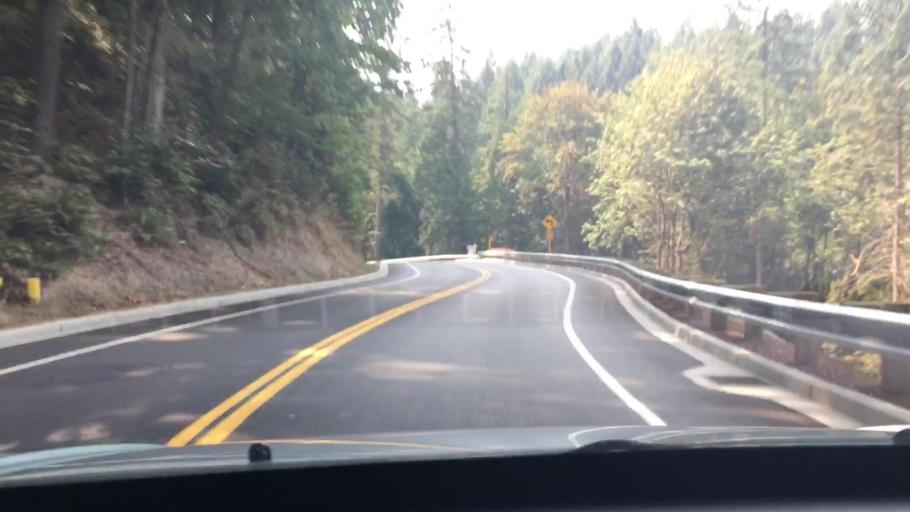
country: US
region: Washington
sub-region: King County
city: City of Sammamish
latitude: 47.5774
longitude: -122.0570
